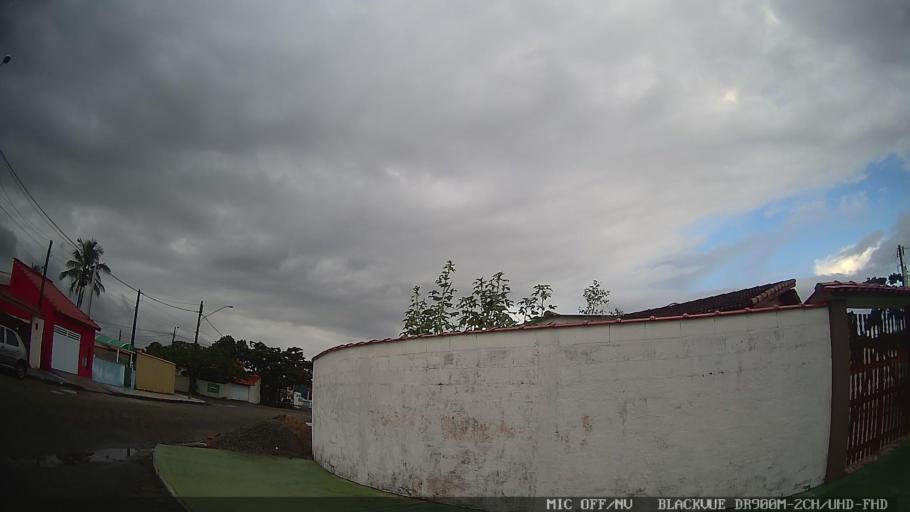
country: BR
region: Sao Paulo
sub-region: Itanhaem
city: Itanhaem
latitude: -24.1801
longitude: -46.7928
